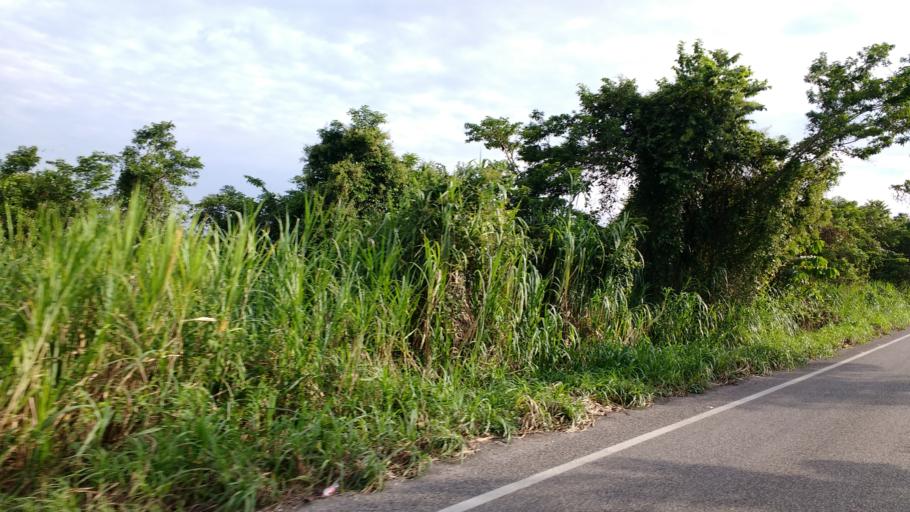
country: MX
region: Tabasco
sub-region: Teapa
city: Eureka y Belen
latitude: 17.6739
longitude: -92.9470
